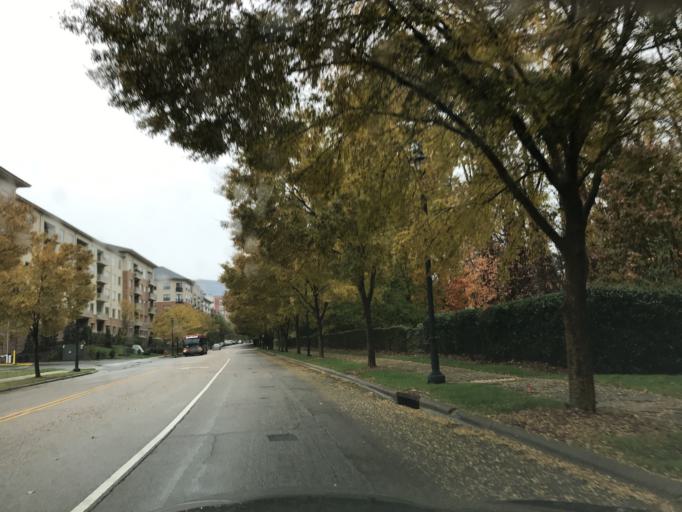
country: US
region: North Carolina
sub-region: Wake County
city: West Raleigh
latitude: 35.8365
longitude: -78.6340
